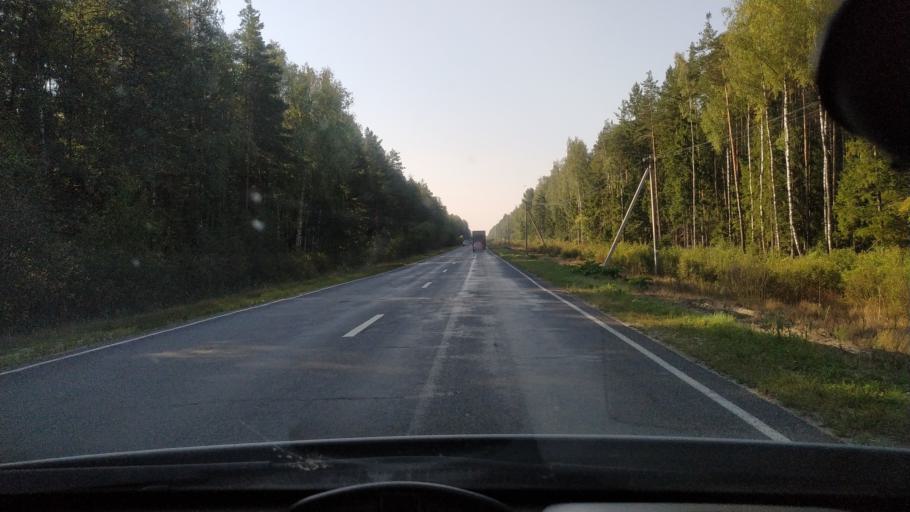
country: RU
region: Moskovskaya
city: Tugolesskiy Bor
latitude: 55.5135
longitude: 39.7120
